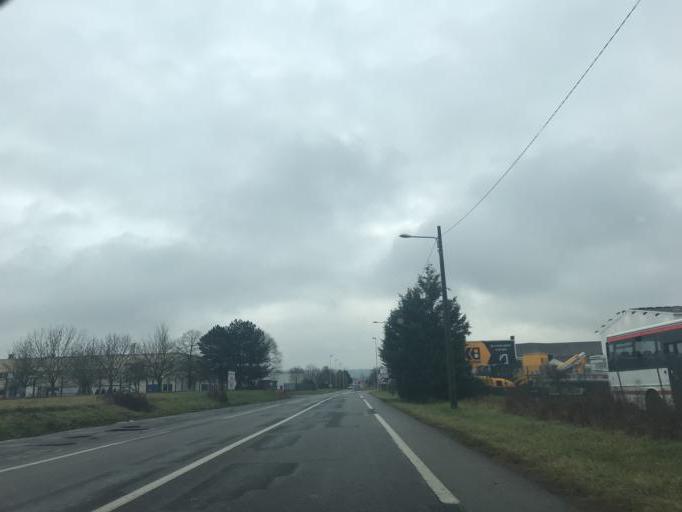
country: FR
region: Rhone-Alpes
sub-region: Departement du Rhone
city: Genay
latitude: 45.8941
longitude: 4.8224
